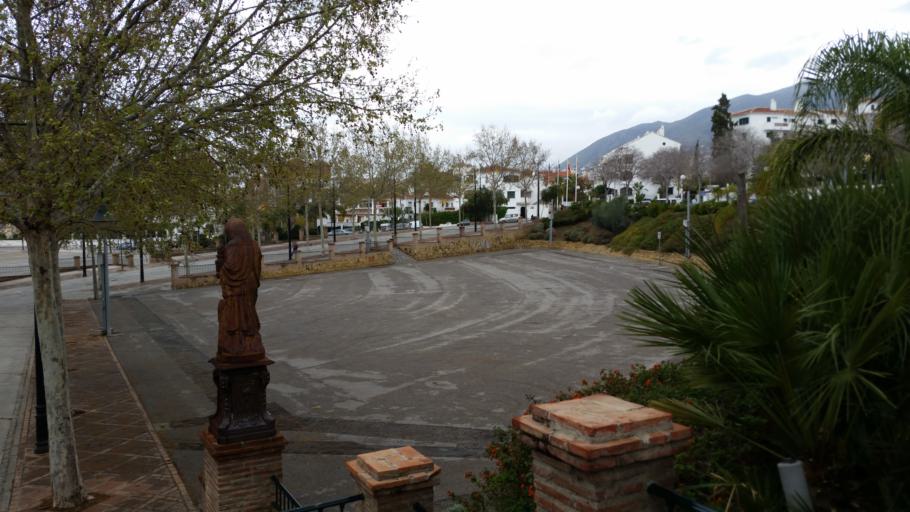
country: ES
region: Andalusia
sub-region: Provincia de Malaga
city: Benalmadena
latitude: 36.5947
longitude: -4.5321
